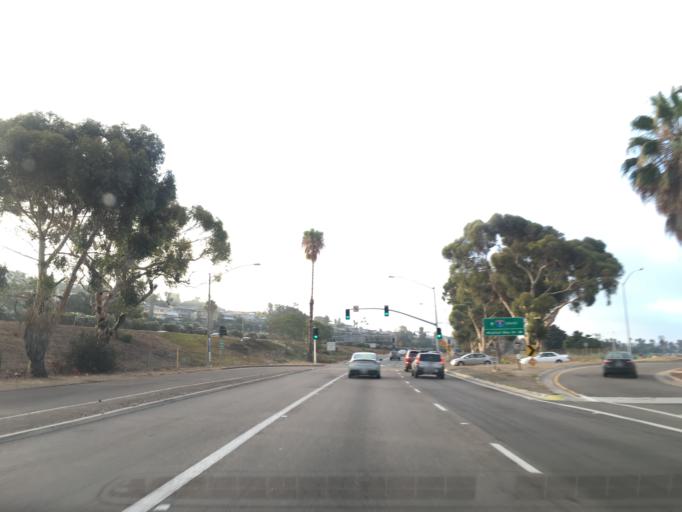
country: US
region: California
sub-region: San Diego County
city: La Jolla
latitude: 32.7987
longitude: -117.2117
